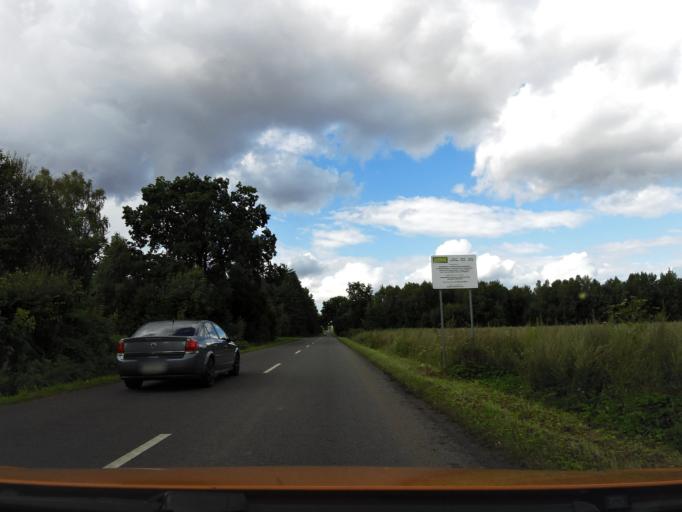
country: PL
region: West Pomeranian Voivodeship
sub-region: Powiat kolobrzeski
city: Ryman
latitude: 53.9632
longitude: 15.4918
